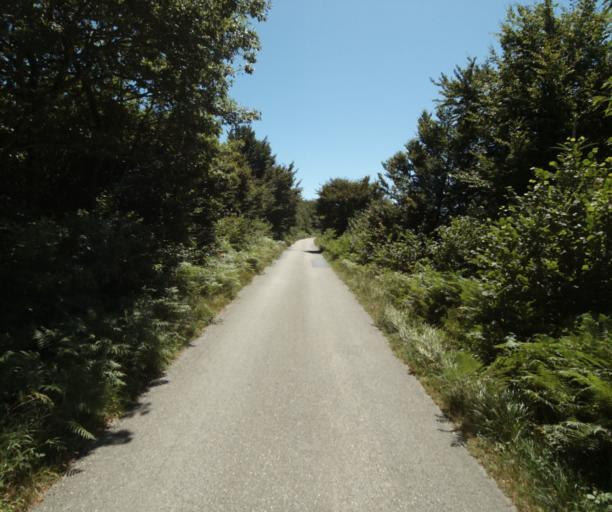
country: FR
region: Languedoc-Roussillon
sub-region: Departement de l'Aude
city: Cuxac-Cabardes
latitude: 43.4081
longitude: 2.2005
